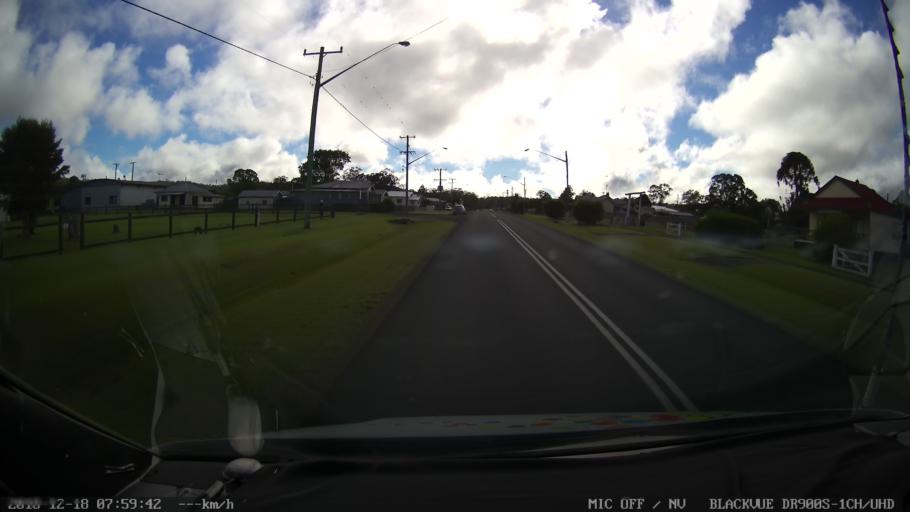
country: AU
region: New South Wales
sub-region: Kyogle
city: Kyogle
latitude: -28.3882
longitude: 152.6071
